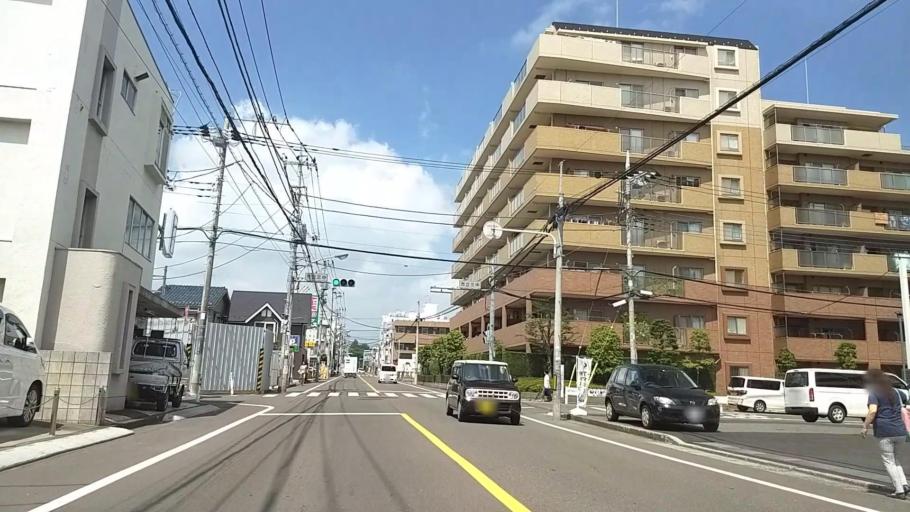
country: JP
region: Tokyo
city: Hachioji
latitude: 35.6516
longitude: 139.3415
